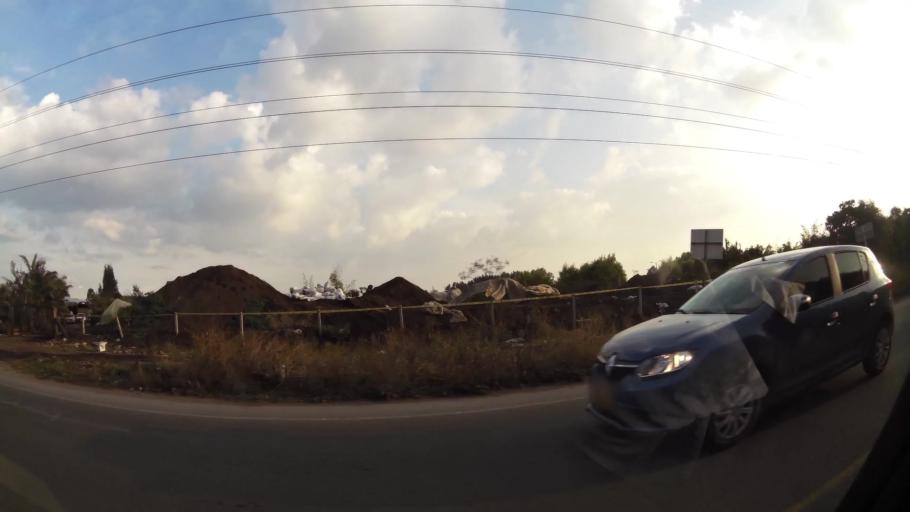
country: CO
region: Cundinamarca
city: Cota
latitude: 4.8005
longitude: -74.1006
